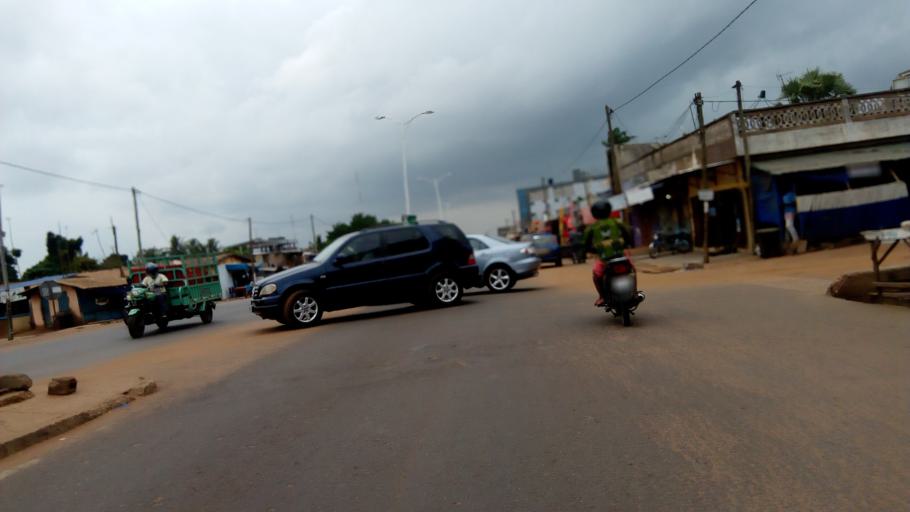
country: TG
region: Maritime
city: Lome
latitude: 6.2289
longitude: 1.2109
